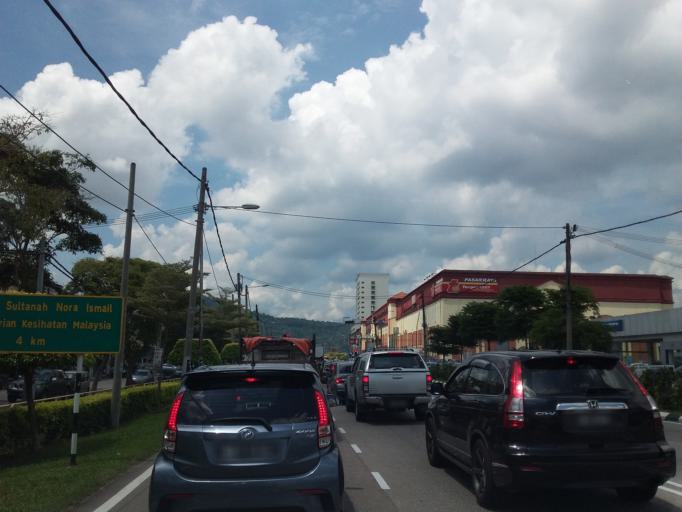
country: MY
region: Johor
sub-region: Daerah Batu Pahat
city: Batu Pahat
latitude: 1.8586
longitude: 102.9323
